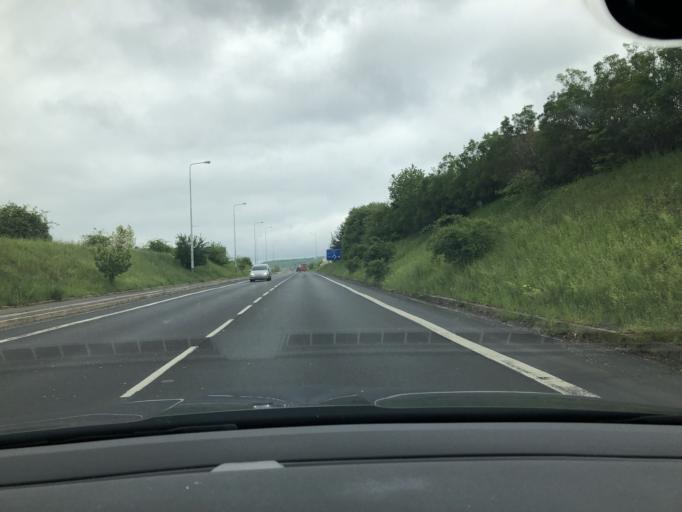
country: CZ
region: Ustecky
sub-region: Okres Usti nad Labem
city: Usti nad Labem
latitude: 50.6902
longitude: 14.0183
